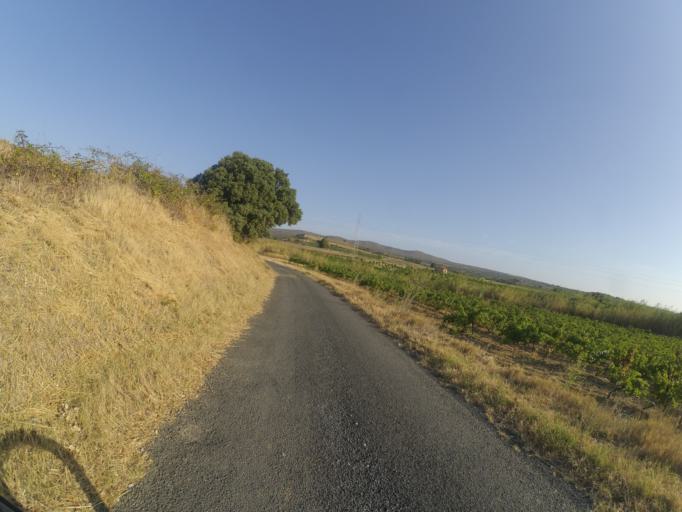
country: FR
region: Languedoc-Roussillon
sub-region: Departement des Pyrenees-Orientales
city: Baixas
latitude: 42.7387
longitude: 2.7777
